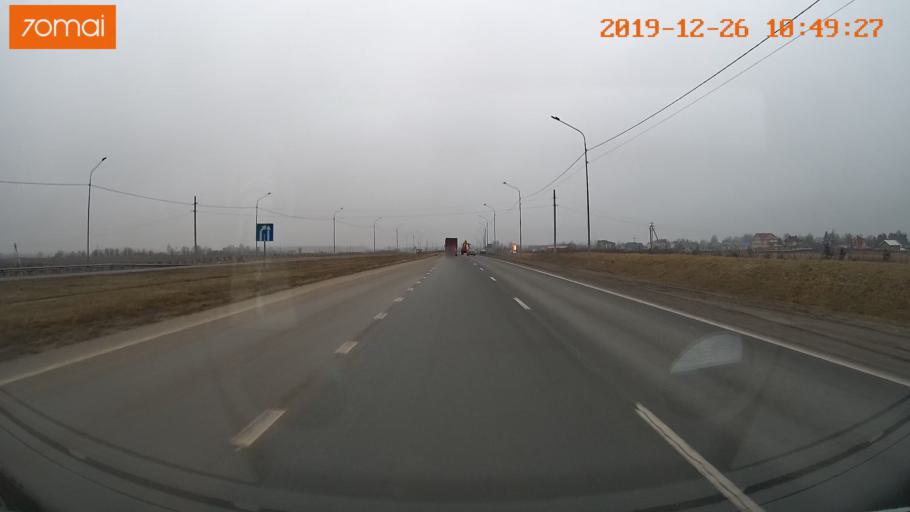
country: RU
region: Vologda
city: Molochnoye
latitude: 59.2112
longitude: 39.7144
